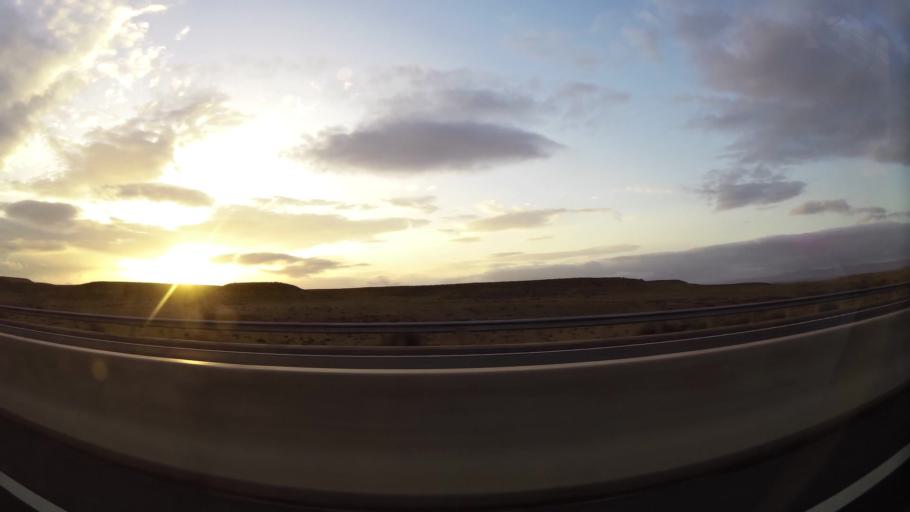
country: MA
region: Oriental
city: Taourirt
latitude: 34.5020
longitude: -2.9544
